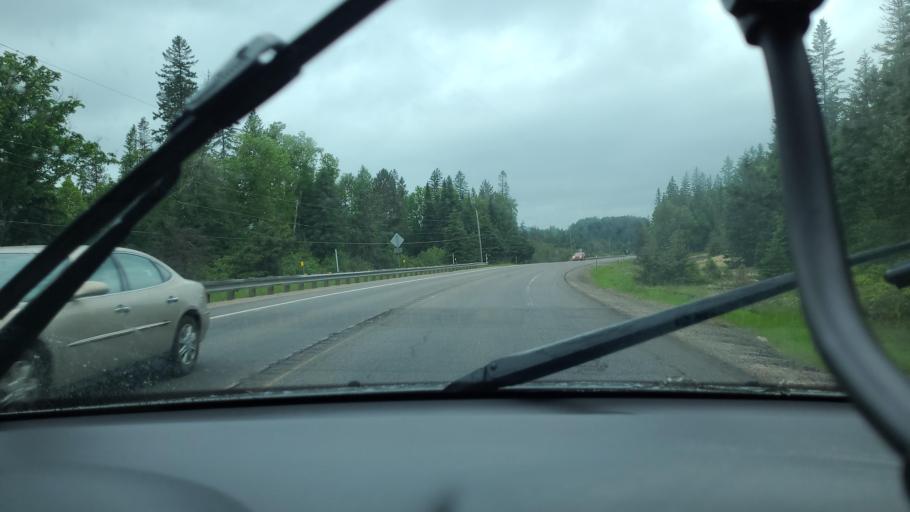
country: CA
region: Quebec
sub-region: Laurentides
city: Riviere-Rouge
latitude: 46.3709
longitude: -74.8476
